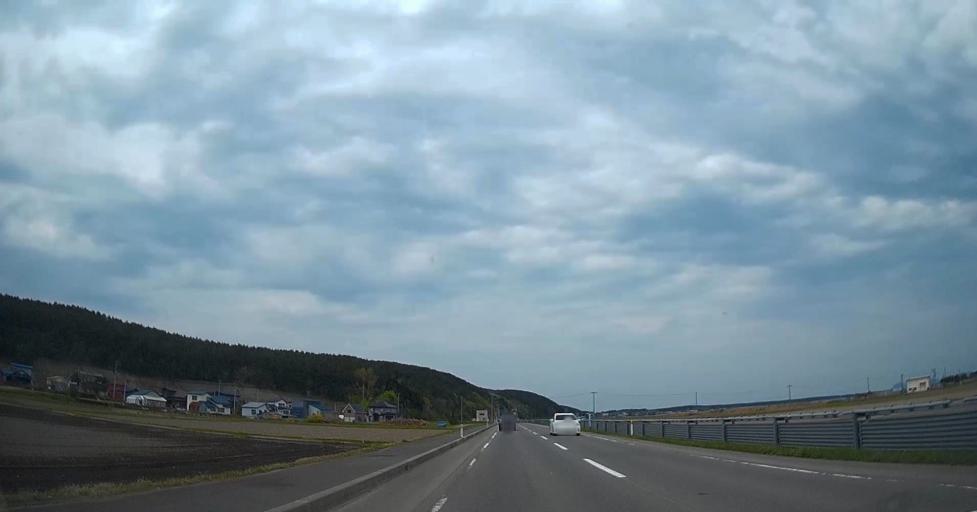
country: JP
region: Aomori
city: Shimokizukuri
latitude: 40.9937
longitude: 140.3588
